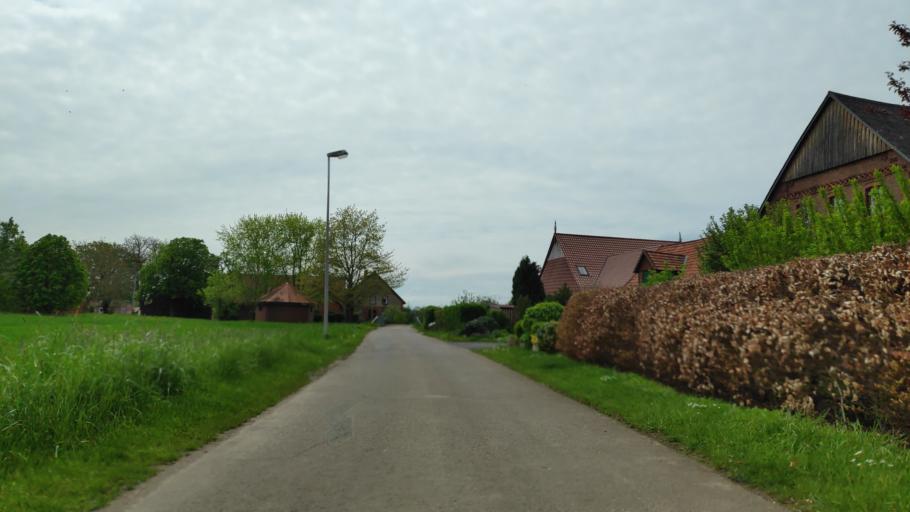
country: DE
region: North Rhine-Westphalia
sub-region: Regierungsbezirk Detmold
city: Petershagen
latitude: 52.3155
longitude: 8.9933
